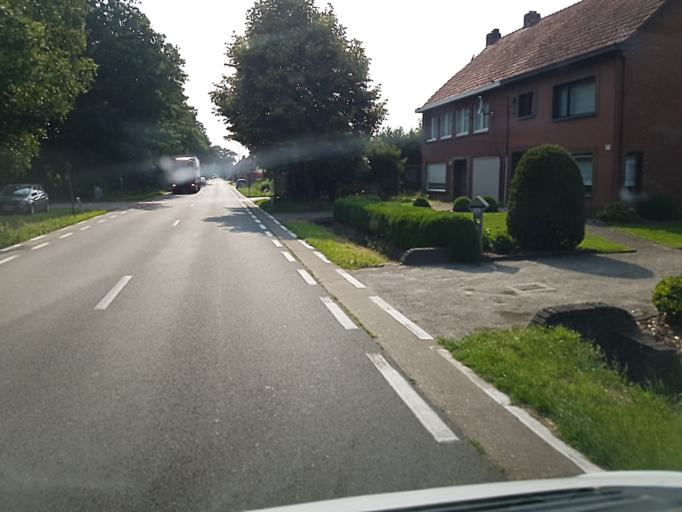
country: BE
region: Flanders
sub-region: Provincie Antwerpen
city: Baarle-Hertog
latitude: 51.3910
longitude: 4.9293
